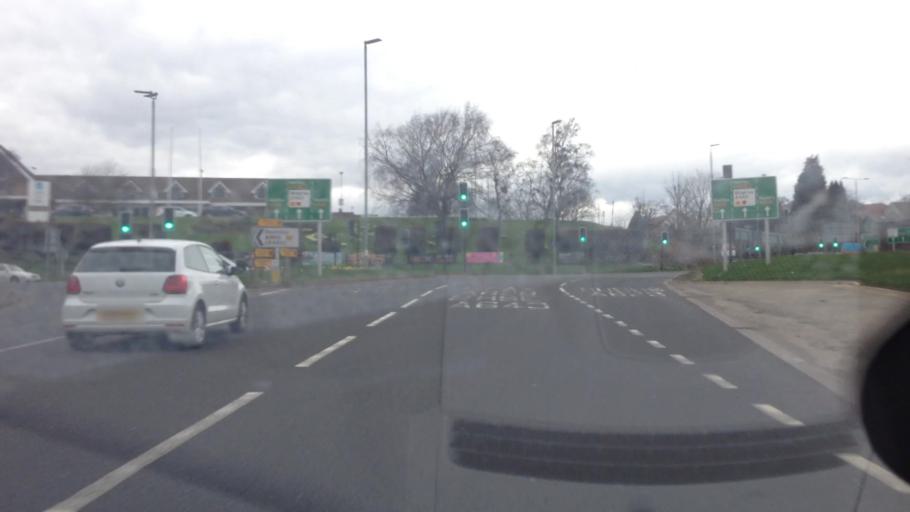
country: GB
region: England
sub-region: Calderdale
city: Elland
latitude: 53.6693
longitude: -1.8274
